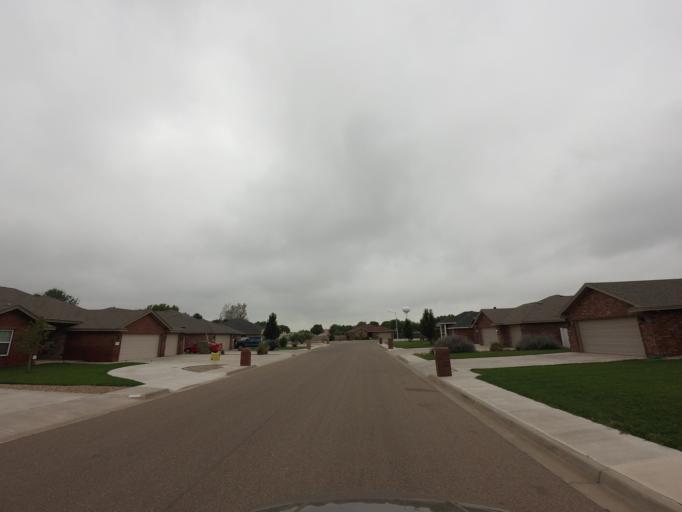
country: US
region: New Mexico
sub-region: Curry County
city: Clovis
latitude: 34.4307
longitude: -103.1807
